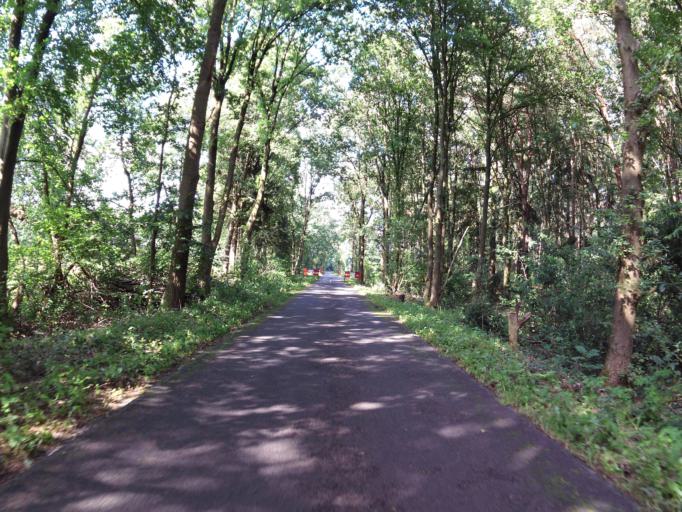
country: NL
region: North Brabant
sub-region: Gemeente Heeze-Leende
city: Heeze
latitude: 51.3812
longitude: 5.5488
